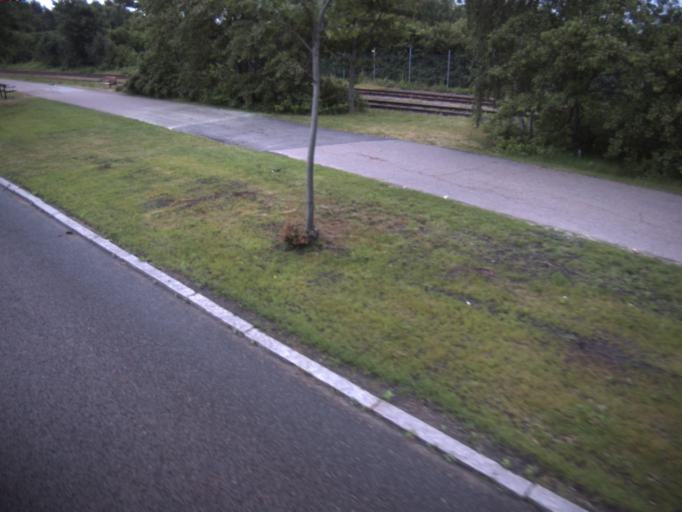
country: SE
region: Skane
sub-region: Helsingborg
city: Helsingborg
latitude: 56.0111
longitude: 12.7200
